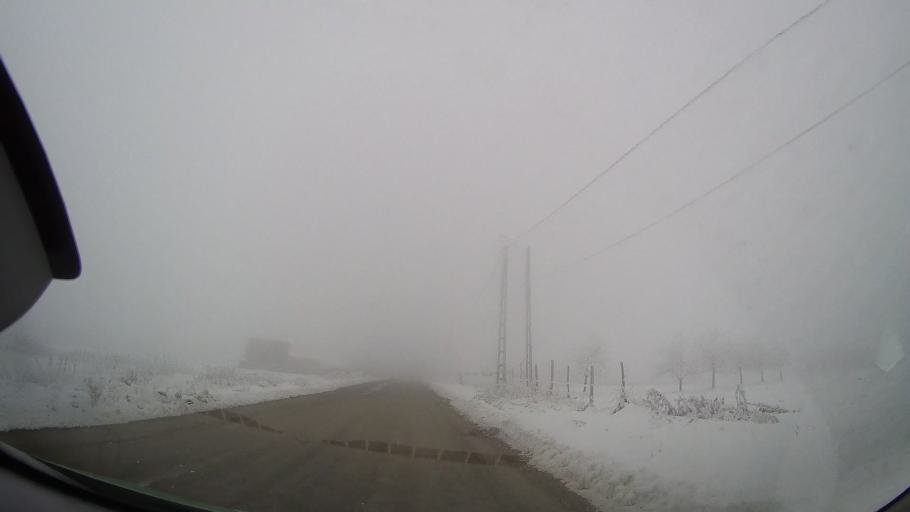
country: RO
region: Iasi
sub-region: Comuna Tansa
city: Suhulet
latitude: 46.8948
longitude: 27.2671
